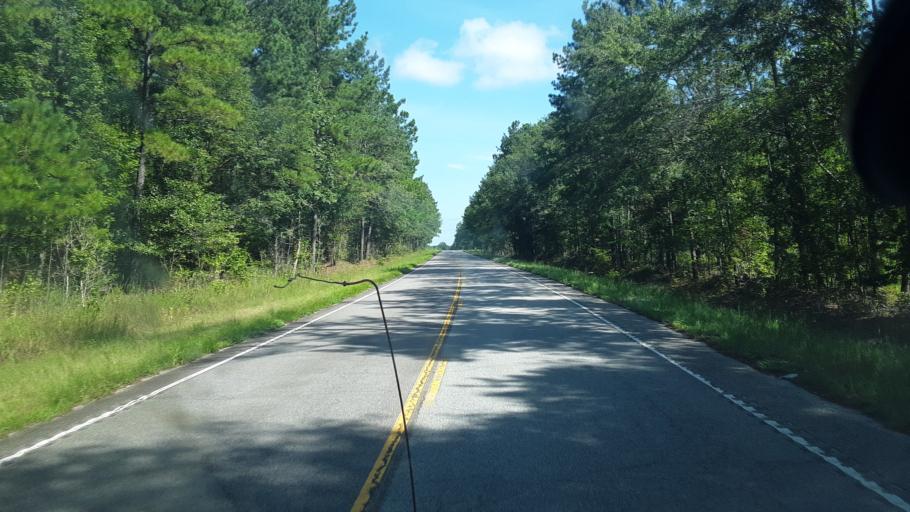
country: US
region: South Carolina
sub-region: Hampton County
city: Varnville
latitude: 32.8029
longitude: -81.0520
